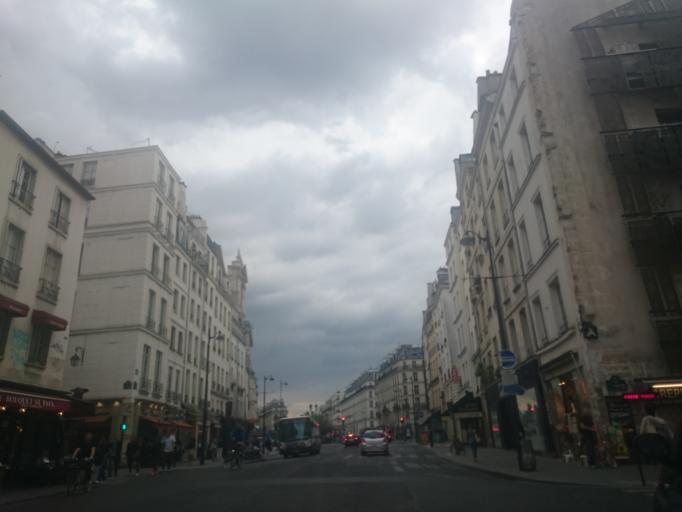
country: FR
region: Ile-de-France
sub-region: Paris
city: Paris
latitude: 48.8545
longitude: 2.3631
